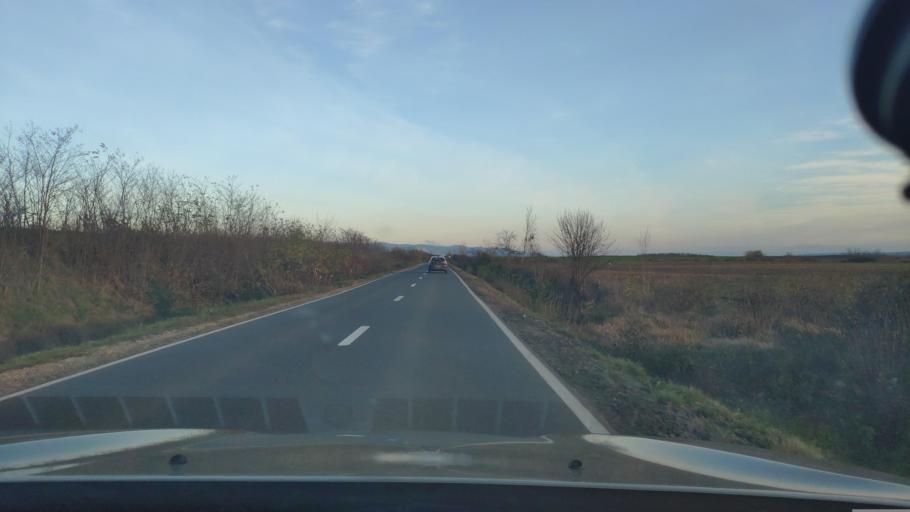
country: RO
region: Satu Mare
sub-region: Comuna Mediesu Aurit
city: Mediesu Aurit
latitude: 47.7703
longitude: 23.1450
